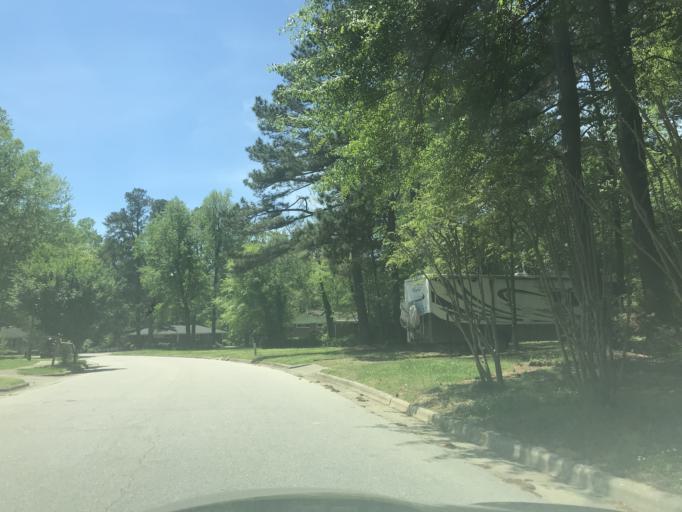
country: US
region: North Carolina
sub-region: Wake County
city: Raleigh
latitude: 35.8281
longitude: -78.5796
